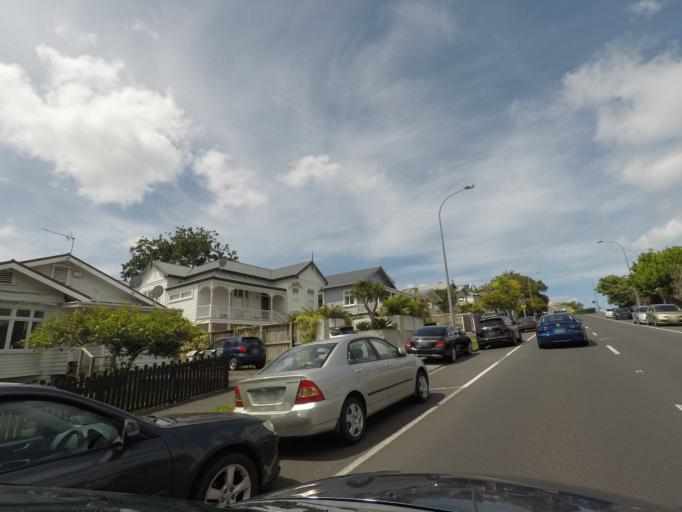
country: NZ
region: Auckland
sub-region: Auckland
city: Auckland
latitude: -36.8495
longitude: 174.7288
